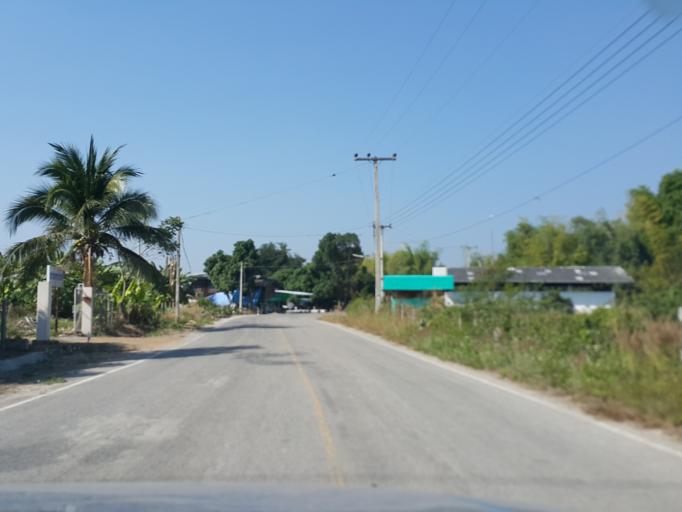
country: TH
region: Chiang Mai
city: Doi Lo
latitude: 18.5301
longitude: 98.7654
